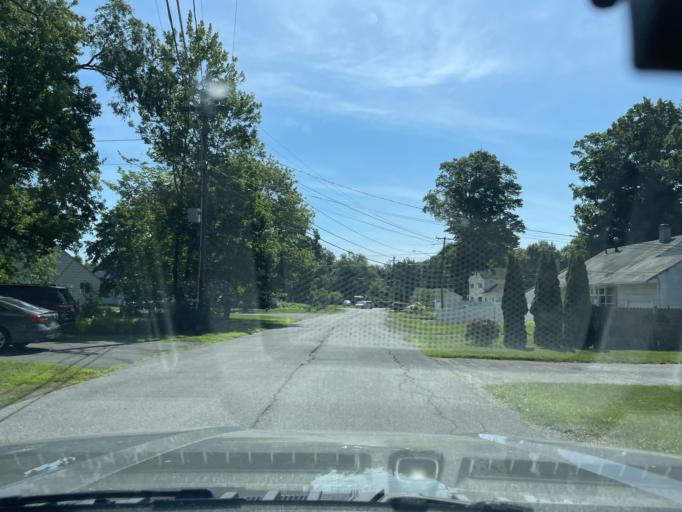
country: US
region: New York
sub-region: Ulster County
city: Saugerties South
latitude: 42.0627
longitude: -73.9551
